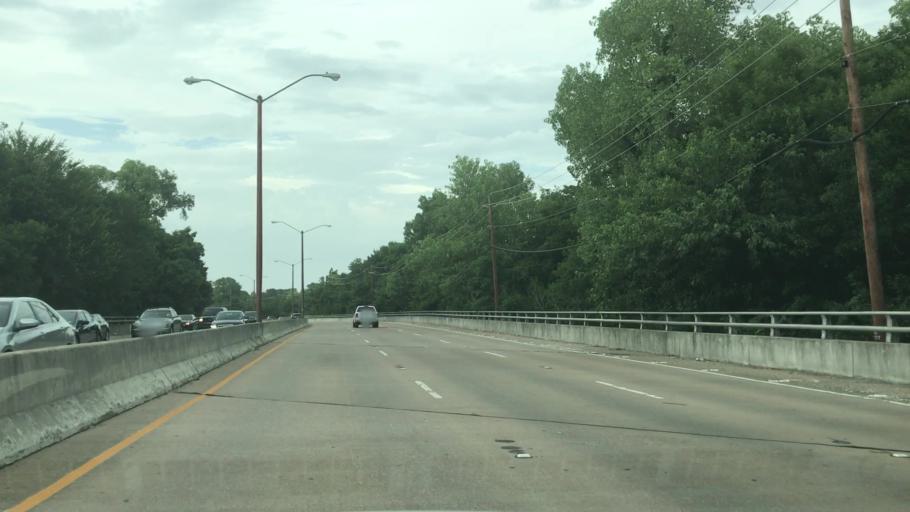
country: US
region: Texas
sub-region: Dallas County
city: University Park
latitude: 32.8705
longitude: -96.7417
